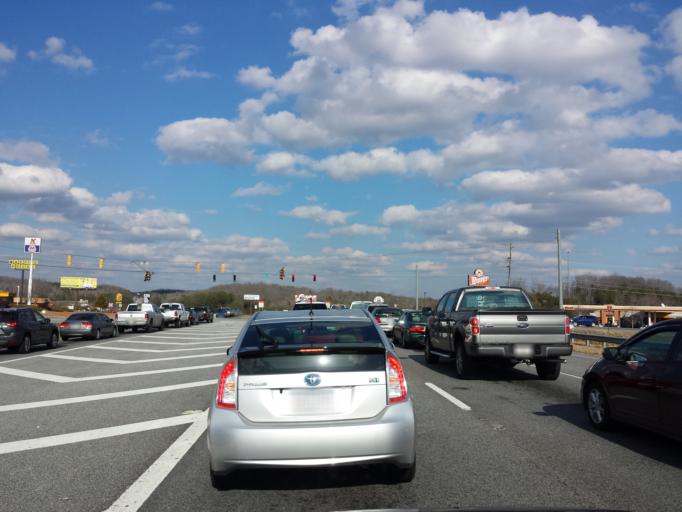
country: US
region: Georgia
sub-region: Dawson County
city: Dawsonville
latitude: 34.3628
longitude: -84.0371
